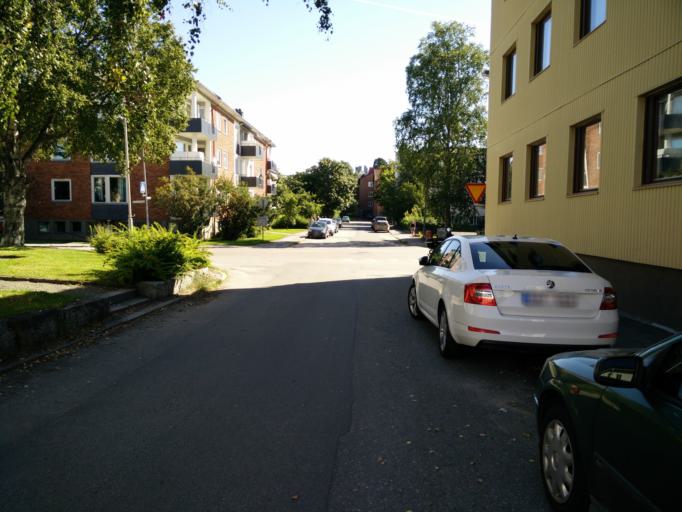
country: SE
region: Vaesternorrland
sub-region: Haernoesands Kommun
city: Haernoesand
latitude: 62.6337
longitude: 17.9453
